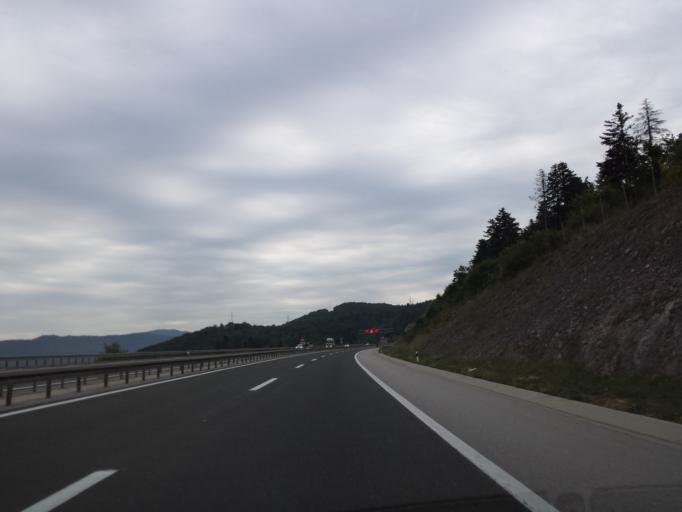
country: HR
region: Licko-Senjska
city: Otocac
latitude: 44.7872
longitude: 15.3340
